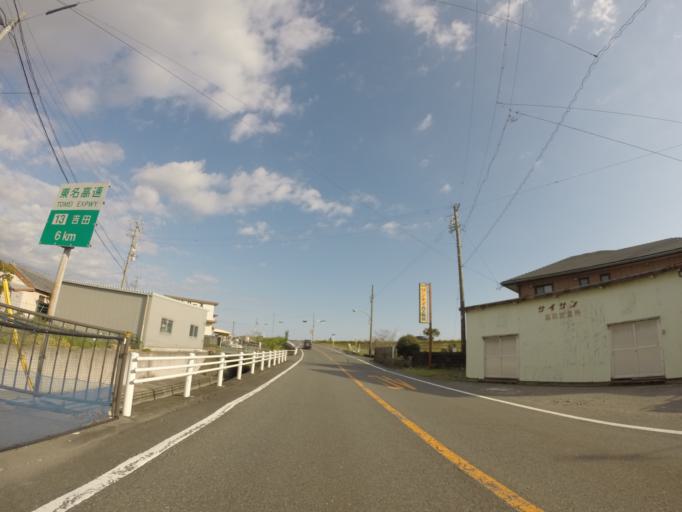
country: JP
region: Shizuoka
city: Shimada
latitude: 34.8292
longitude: 138.1957
